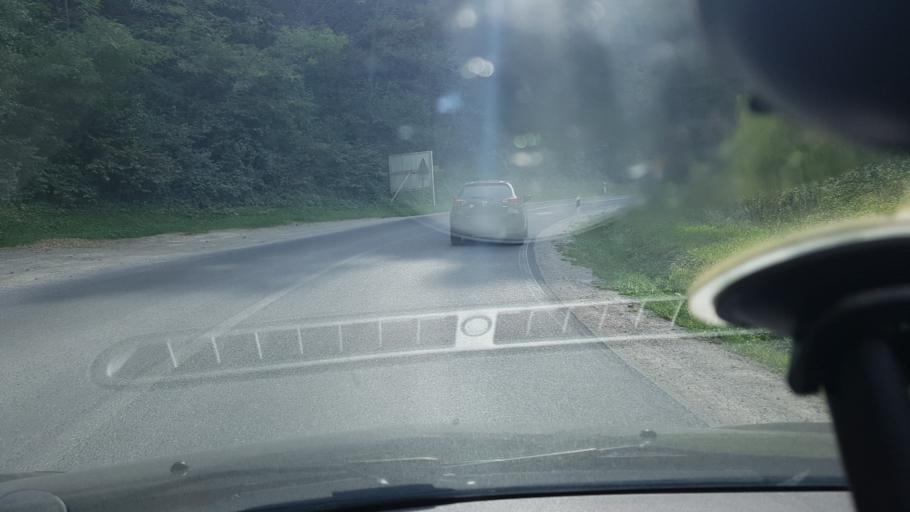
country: HR
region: Varazdinska
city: Lepoglava
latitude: 46.1918
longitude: 15.9889
